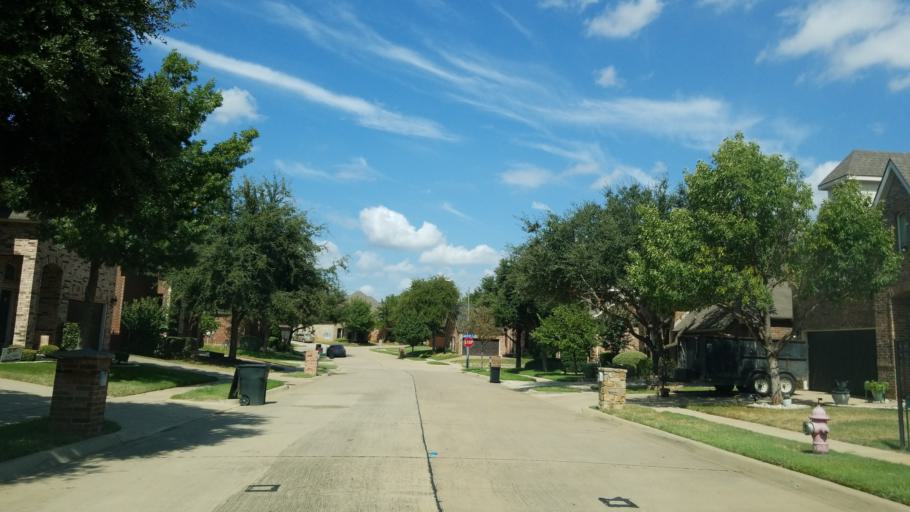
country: US
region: Texas
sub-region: Tarrant County
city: Euless
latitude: 32.8601
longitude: -97.0969
